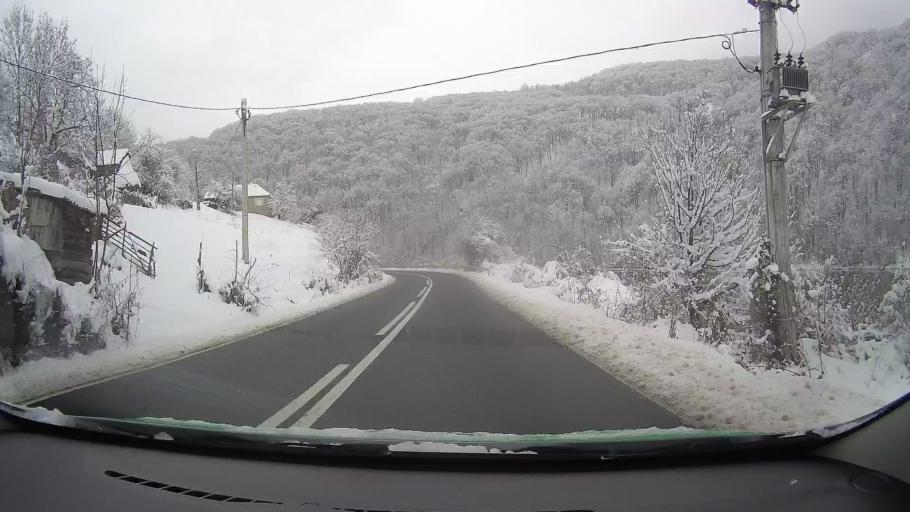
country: RO
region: Alba
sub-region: Comuna Sugag
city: Sugag
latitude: 45.8145
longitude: 23.6136
